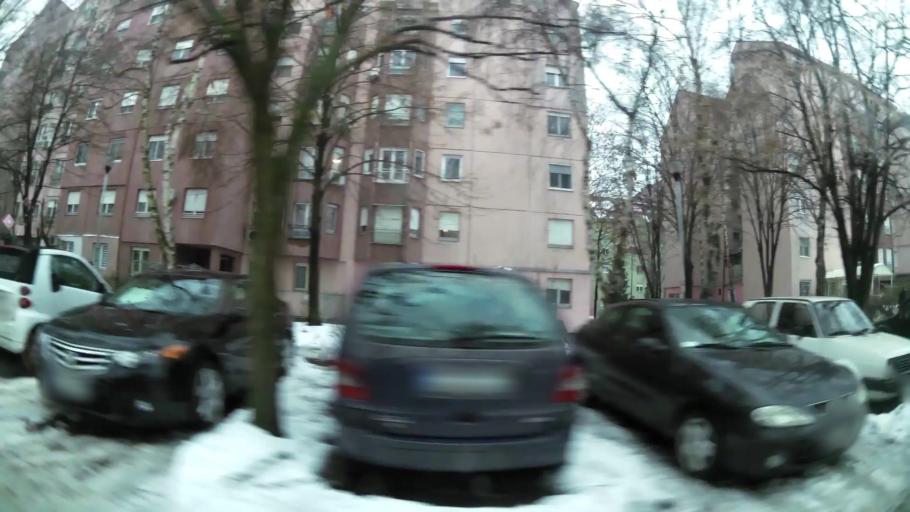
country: RS
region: Central Serbia
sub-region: Belgrade
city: Zemun
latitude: 44.8155
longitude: 20.3756
